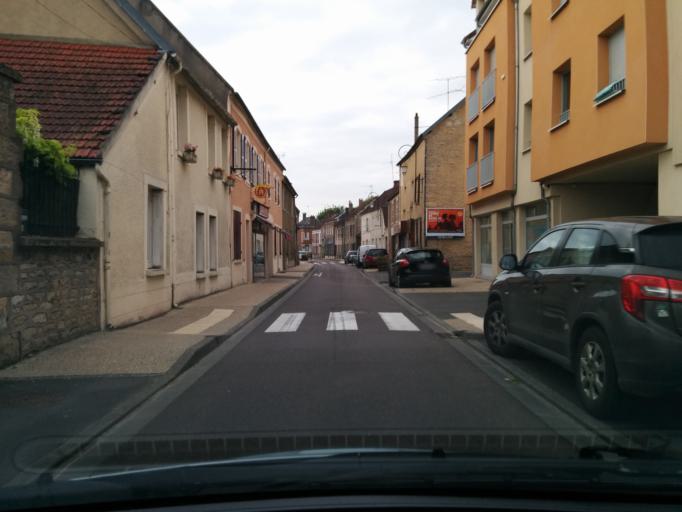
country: FR
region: Haute-Normandie
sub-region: Departement de l'Eure
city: Gasny
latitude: 49.0911
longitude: 1.6051
